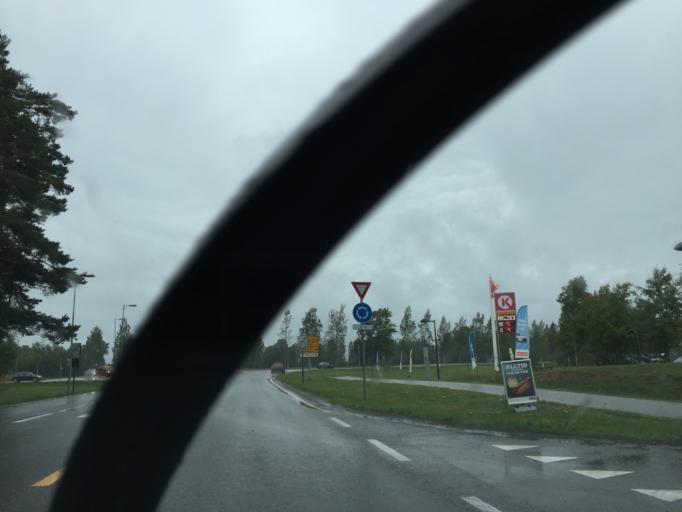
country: NO
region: Akershus
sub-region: Nannestad
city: Teigebyen
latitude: 60.1794
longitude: 11.0827
